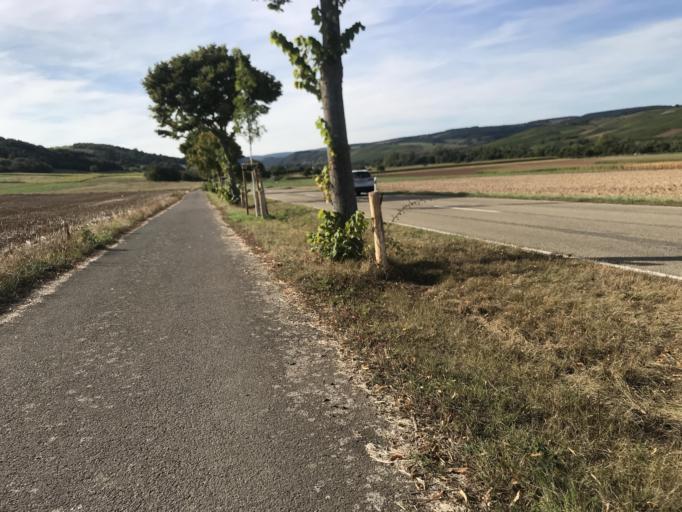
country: DE
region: Rheinland-Pfalz
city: Monzingen
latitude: 49.7867
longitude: 7.5869
